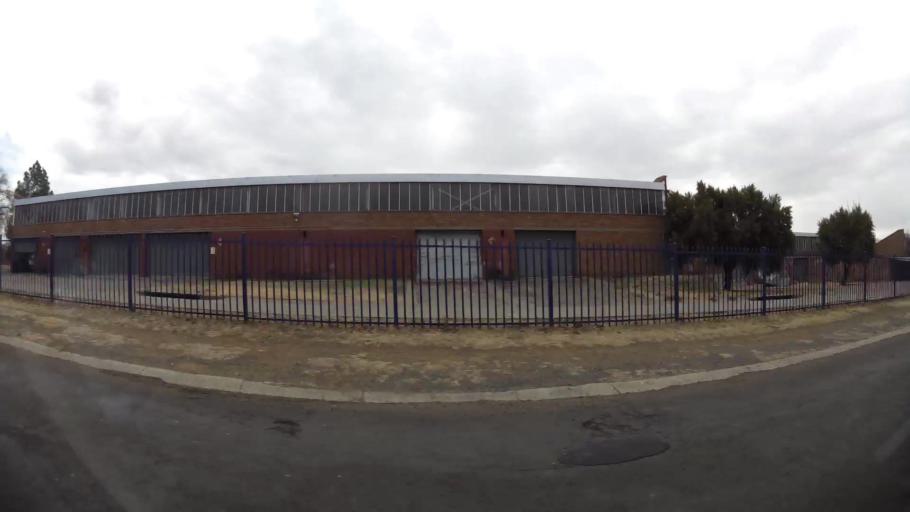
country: ZA
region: Orange Free State
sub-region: Fezile Dabi District Municipality
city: Kroonstad
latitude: -27.6367
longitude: 27.2349
